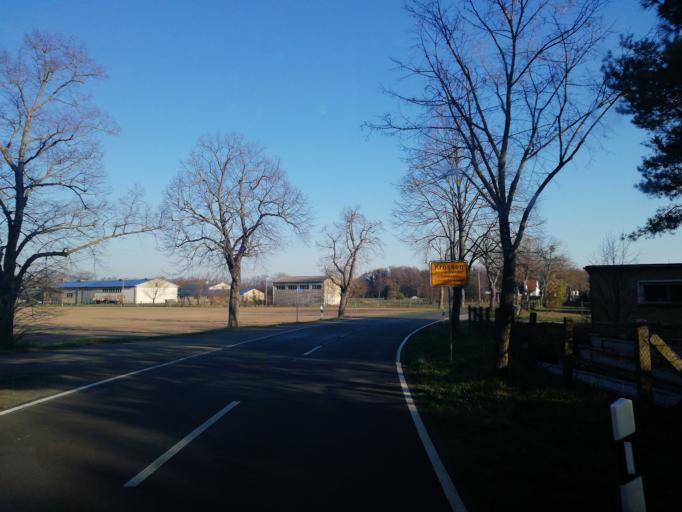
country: DE
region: Brandenburg
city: Drahnsdorf
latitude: 51.9139
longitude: 13.5940
